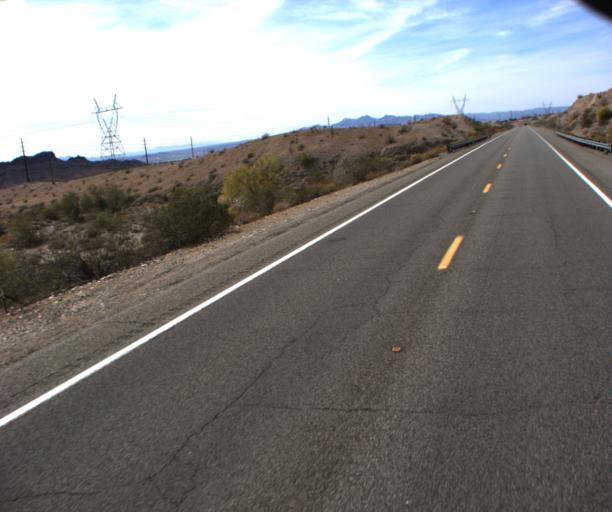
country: US
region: Arizona
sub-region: Mohave County
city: Lake Havasu City
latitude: 34.4447
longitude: -114.2360
